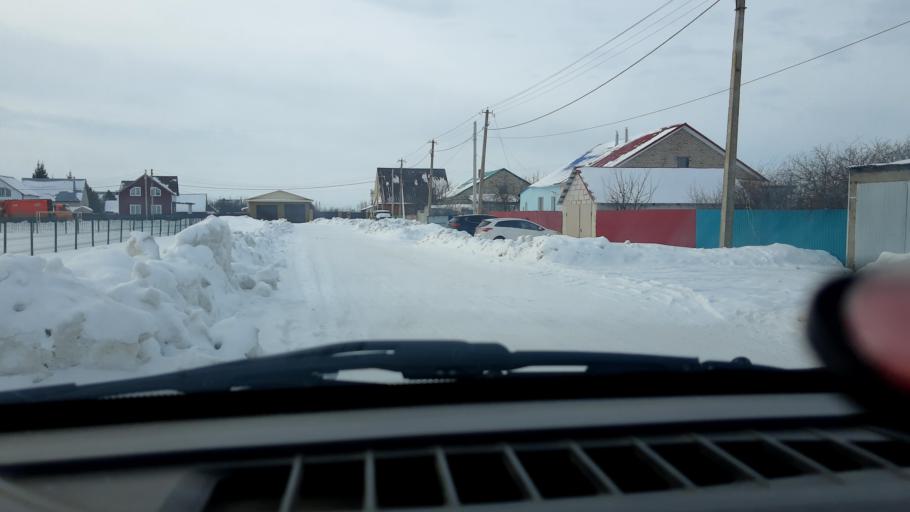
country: RU
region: Bashkortostan
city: Kabakovo
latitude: 54.6004
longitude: 56.1868
